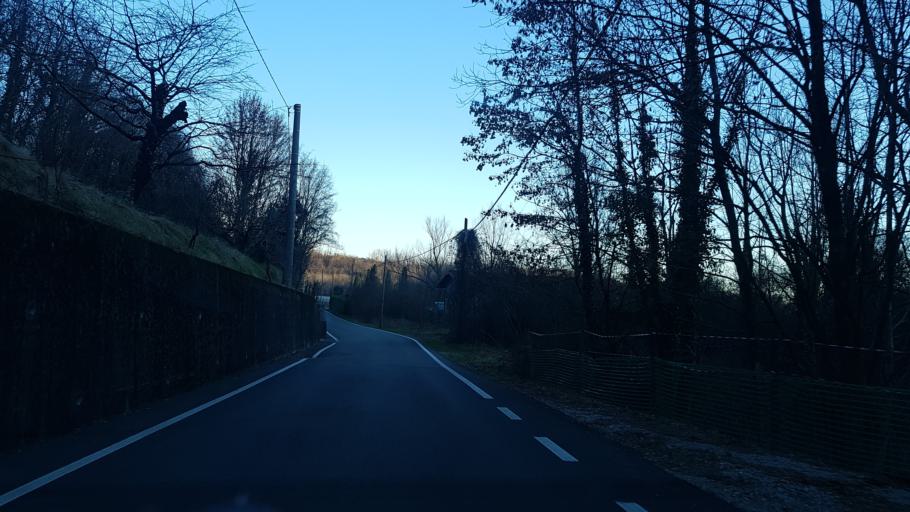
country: IT
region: Friuli Venezia Giulia
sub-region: Provincia di Udine
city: Tarcento
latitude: 46.2316
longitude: 13.2203
